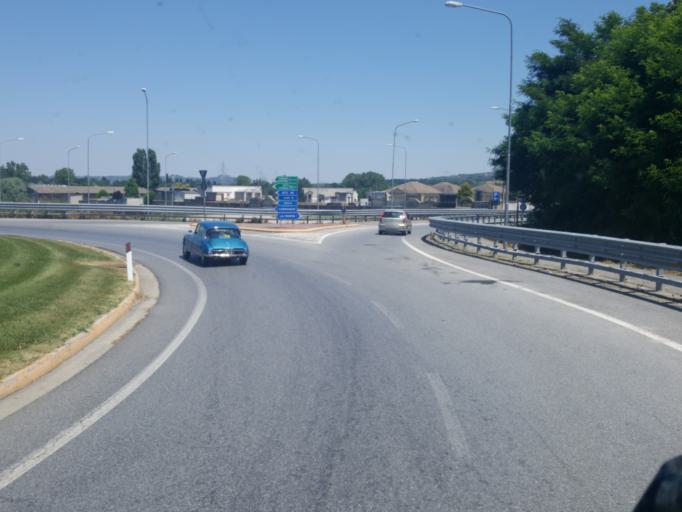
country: IT
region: Piedmont
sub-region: Provincia di Cuneo
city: Cherasco
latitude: 44.6508
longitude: 7.8701
